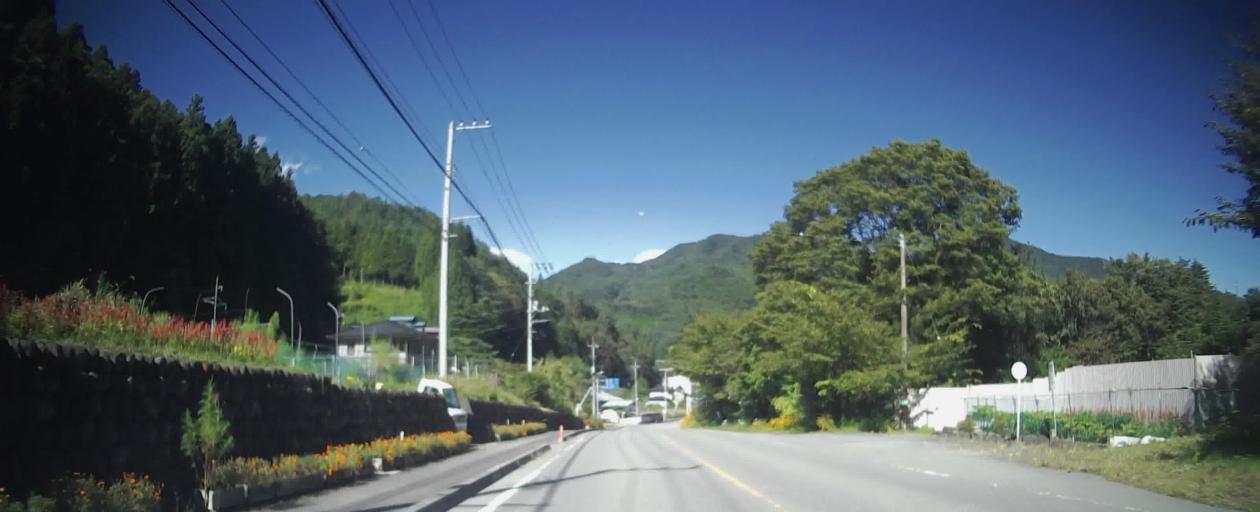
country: JP
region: Gunma
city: Nakanojomachi
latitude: 36.5680
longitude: 138.7298
